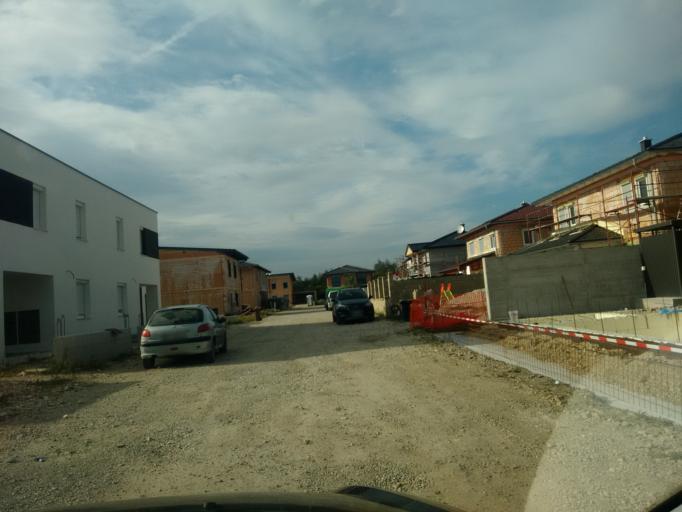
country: AT
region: Upper Austria
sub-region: Wels Stadt
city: Wels
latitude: 48.1663
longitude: 13.9922
